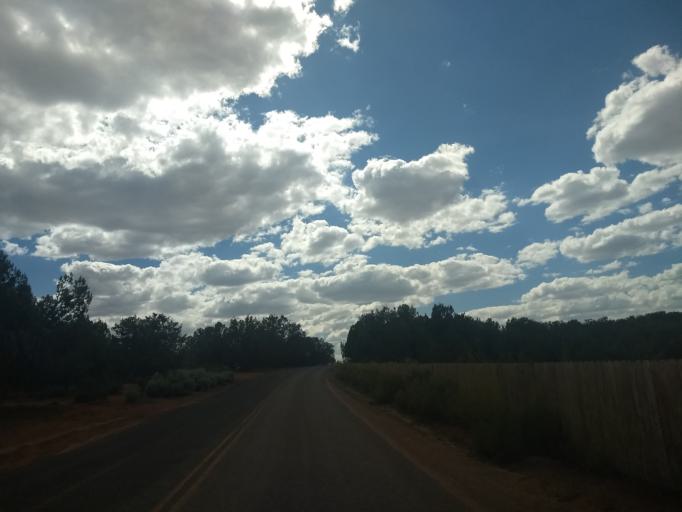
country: US
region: Utah
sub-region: Kane County
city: Kanab
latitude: 37.1470
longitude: -112.5479
